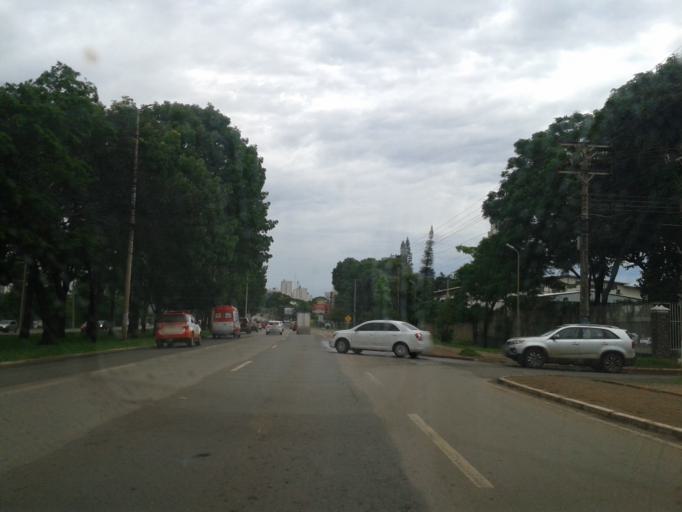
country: BR
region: Federal District
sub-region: Brasilia
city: Brasilia
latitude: -15.8200
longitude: -48.0575
